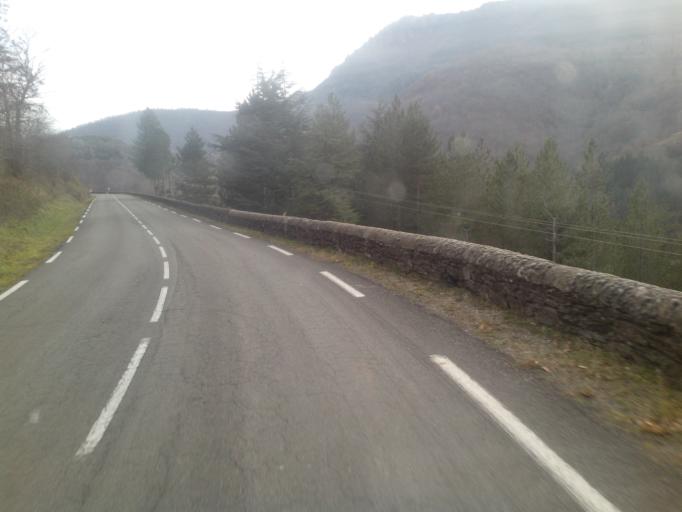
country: FR
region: Languedoc-Roussillon
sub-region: Departement de la Lozere
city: Florac
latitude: 44.3644
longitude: 3.5579
